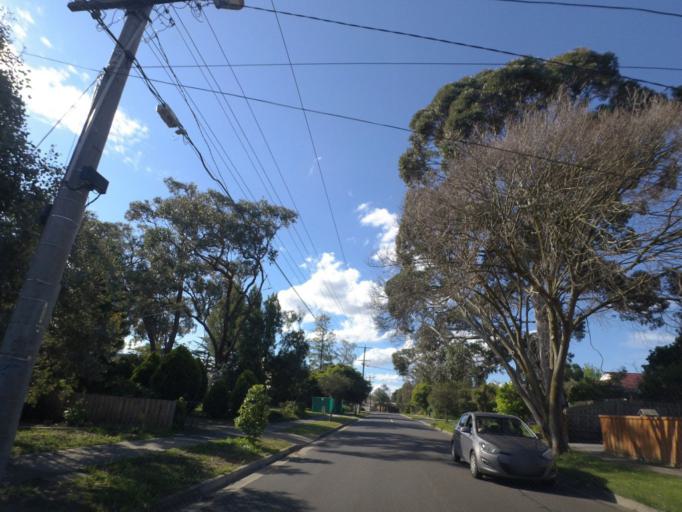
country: AU
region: Victoria
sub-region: Knox
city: Knoxfield
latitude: -37.8872
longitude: 145.2491
